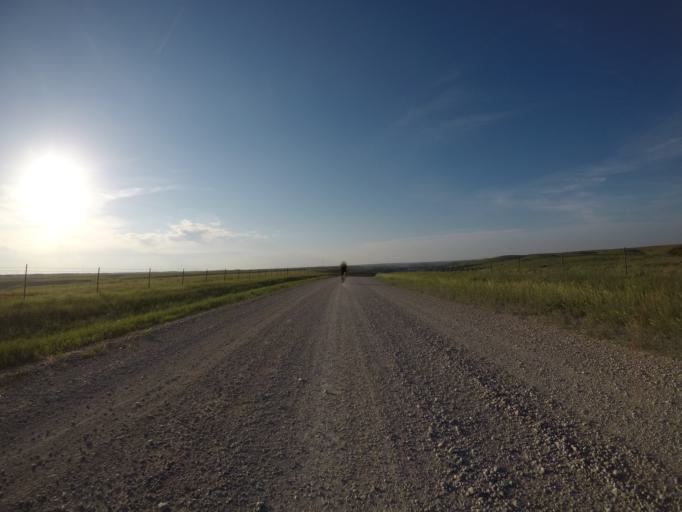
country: US
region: Kansas
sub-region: Riley County
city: Manhattan
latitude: 39.0506
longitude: -96.4956
